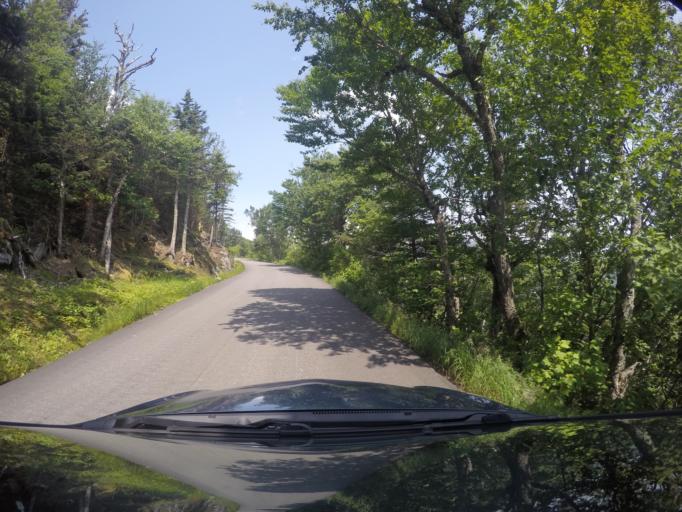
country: US
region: New Hampshire
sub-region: Coos County
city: Gorham
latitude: 44.2828
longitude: -71.2572
